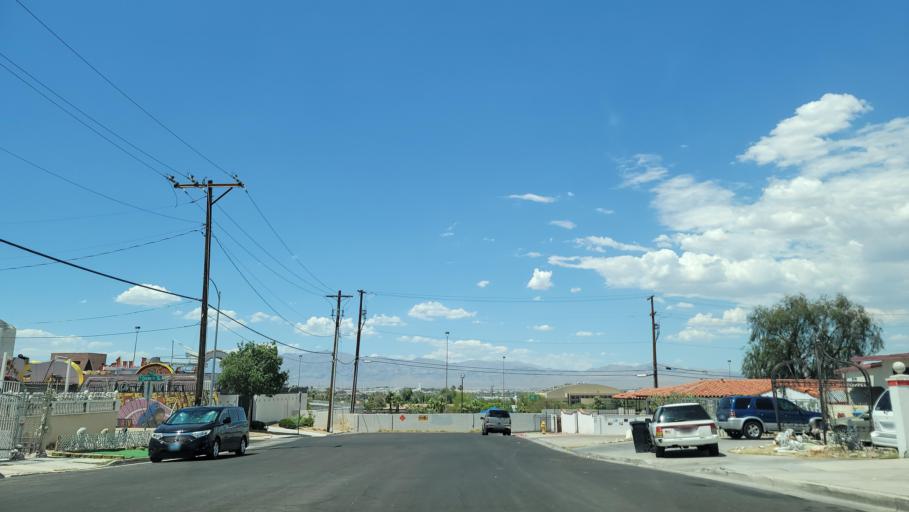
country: US
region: Nevada
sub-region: Clark County
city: Las Vegas
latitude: 36.1768
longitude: -115.1339
